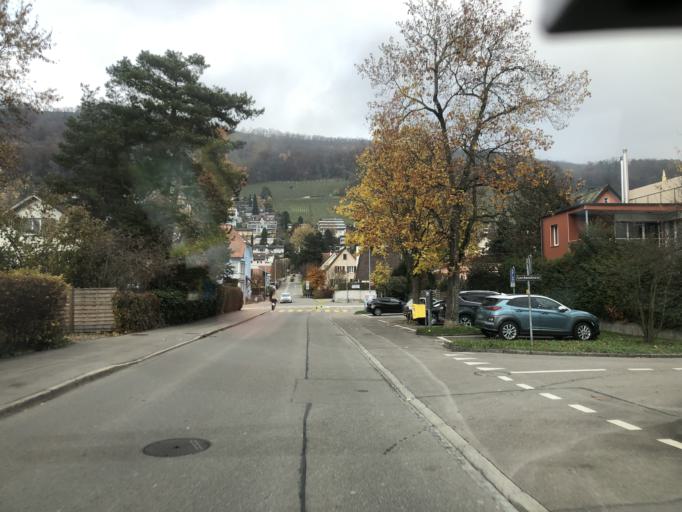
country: CH
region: Aargau
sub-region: Bezirk Baden
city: Wettingen
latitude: 47.4690
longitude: 8.3229
